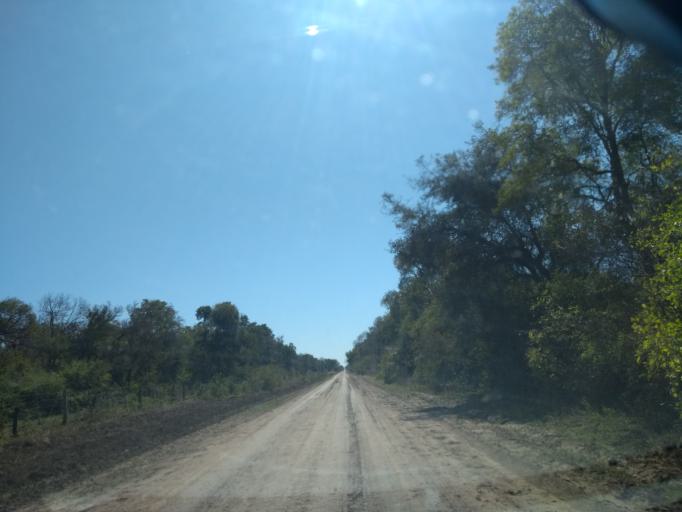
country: AR
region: Chaco
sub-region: Departamento de Quitilipi
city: Quitilipi
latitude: -26.7193
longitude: -60.2267
